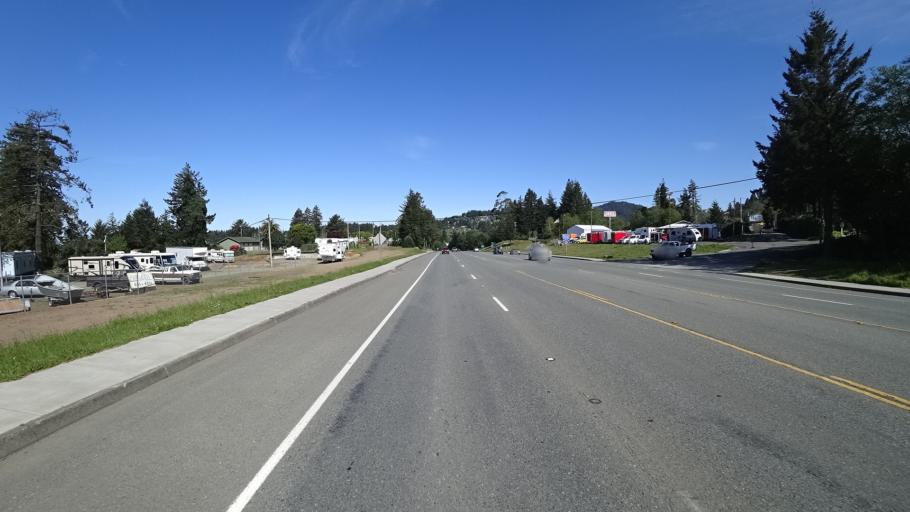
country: US
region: Oregon
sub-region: Curry County
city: Harbor
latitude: 42.0516
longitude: -124.2614
